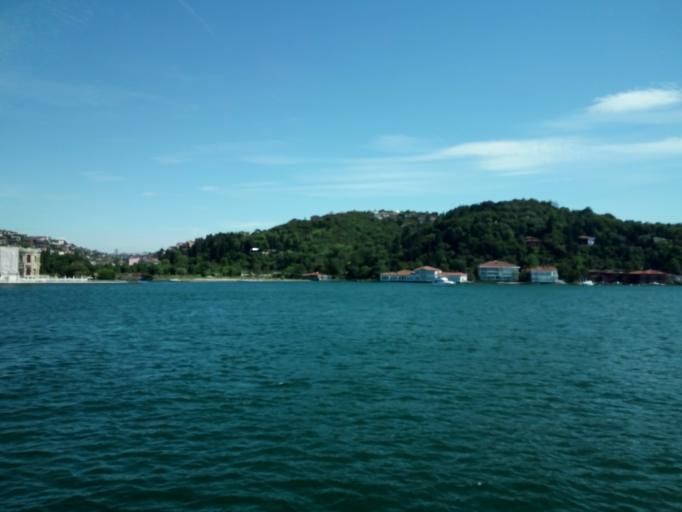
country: TR
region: Istanbul
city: UEskuedar
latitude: 41.0802
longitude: 29.0618
